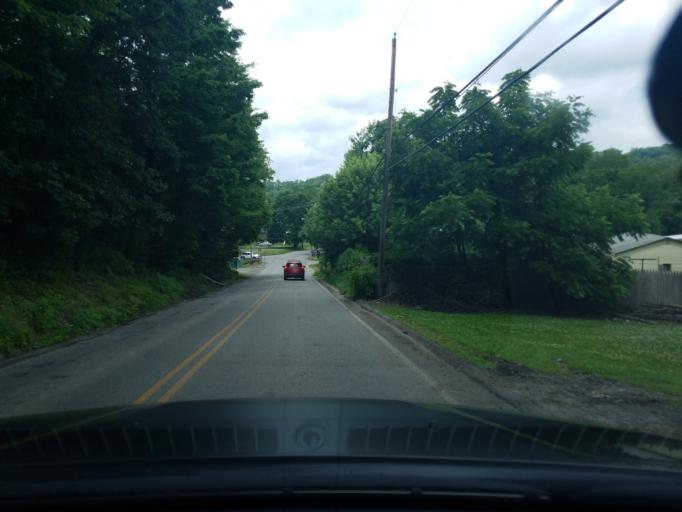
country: US
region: Pennsylvania
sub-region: Westmoreland County
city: Youngwood
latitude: 40.2249
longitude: -79.5860
